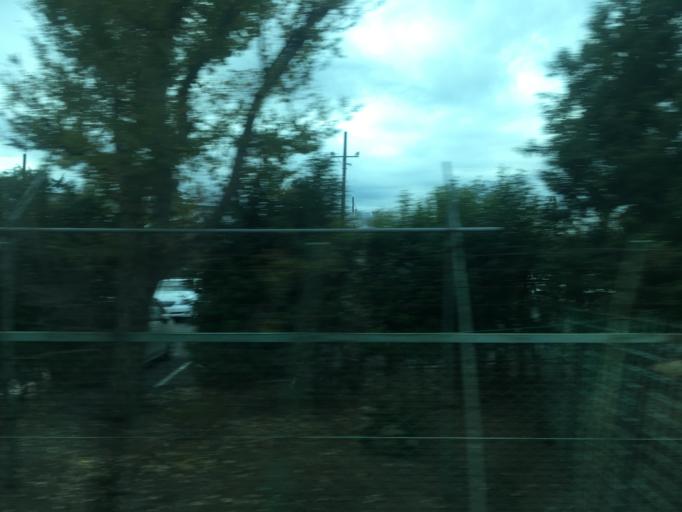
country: JP
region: Saitama
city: Okegawa
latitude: 36.0055
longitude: 139.5567
